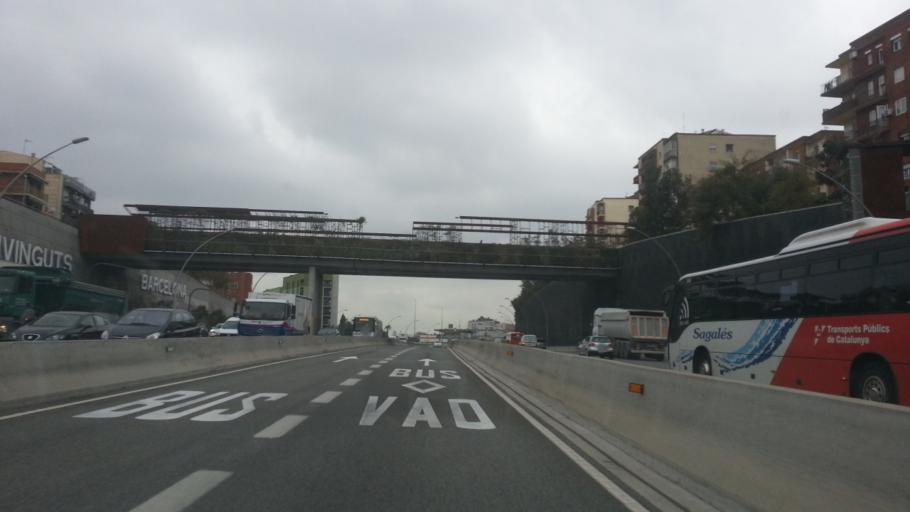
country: ES
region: Catalonia
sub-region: Provincia de Barcelona
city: Nou Barris
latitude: 41.4521
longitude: 2.1891
